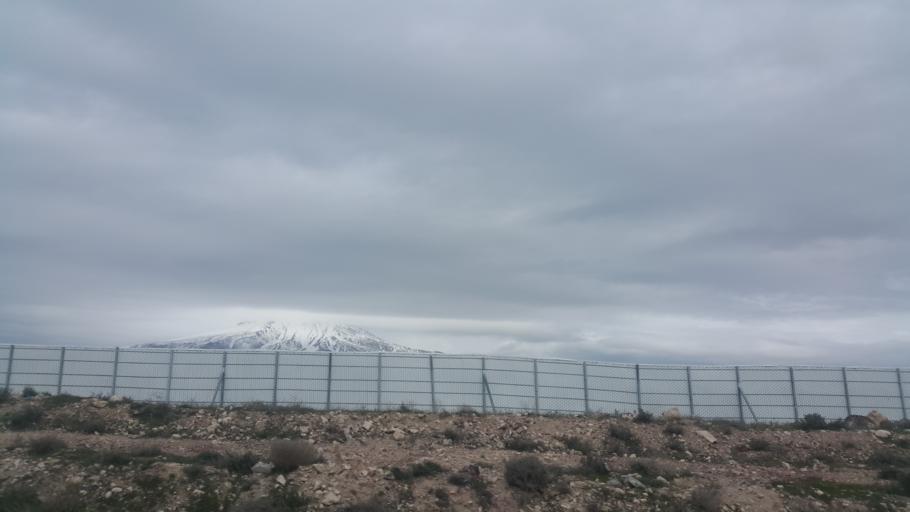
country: TR
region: Aksaray
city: Taspinar
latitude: 38.1069
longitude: 34.0336
